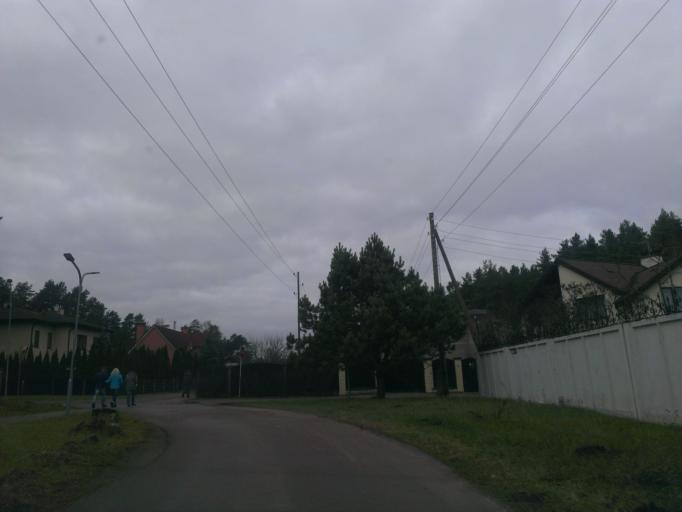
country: LV
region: Riga
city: Bergi
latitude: 56.9916
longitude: 24.3036
